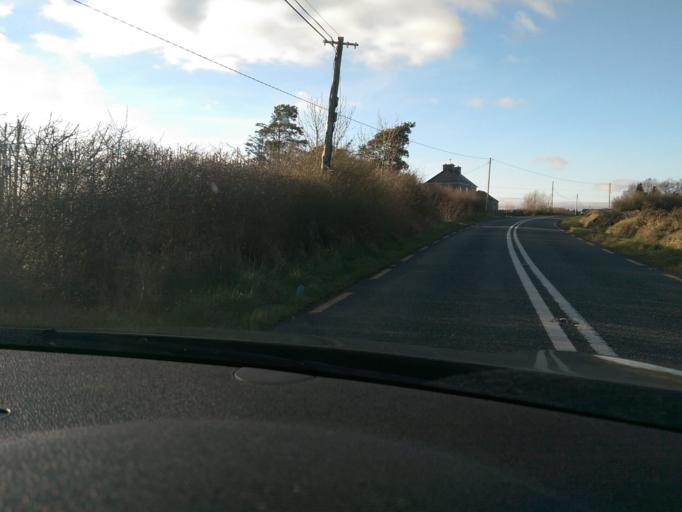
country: IE
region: Connaught
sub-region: Roscommon
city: Boyle
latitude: 53.9123
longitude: -8.2704
